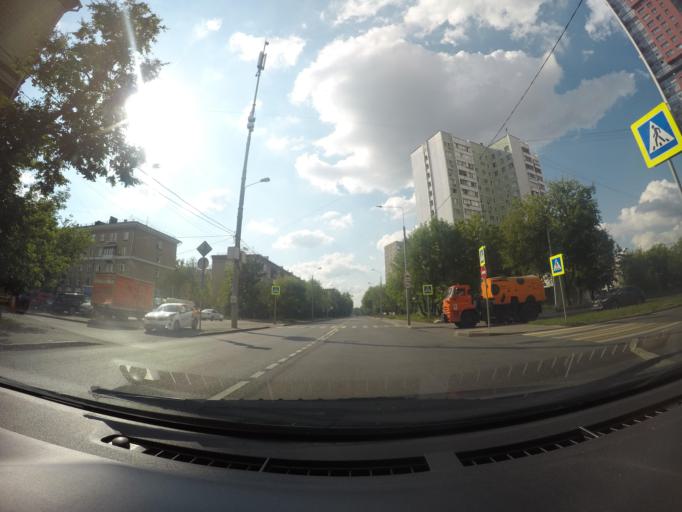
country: RU
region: Moscow
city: Leonovo
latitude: 55.8357
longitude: 37.6432
